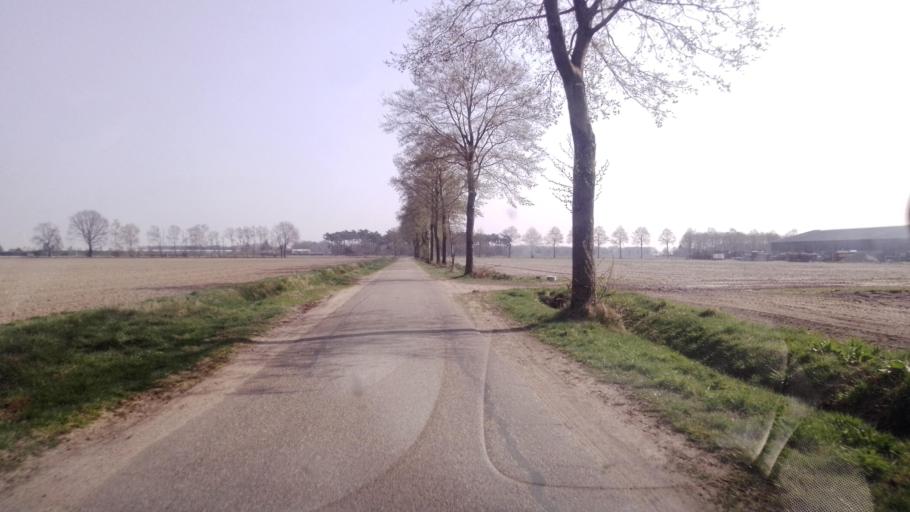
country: NL
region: Limburg
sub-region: Gemeente Peel en Maas
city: Maasbree
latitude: 51.3772
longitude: 6.0402
